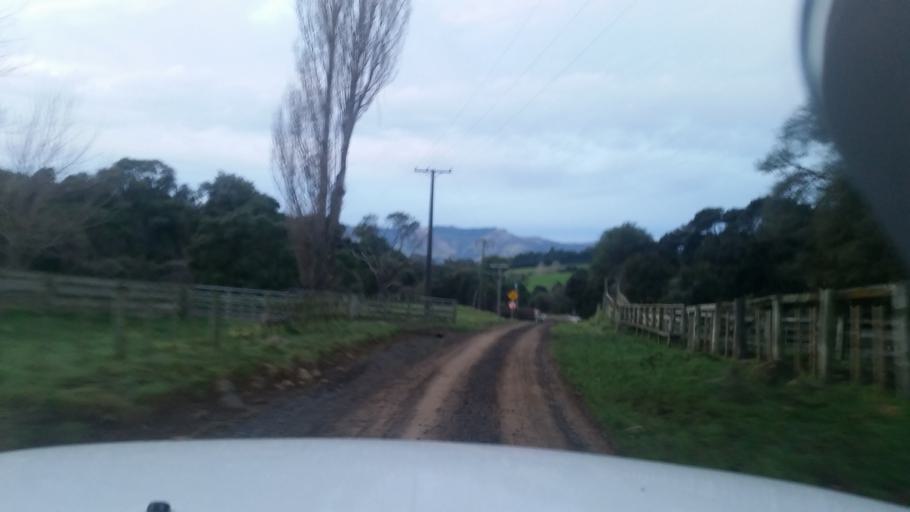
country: NZ
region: Canterbury
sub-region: Christchurch City
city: Christchurch
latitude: -43.7534
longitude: 172.8969
